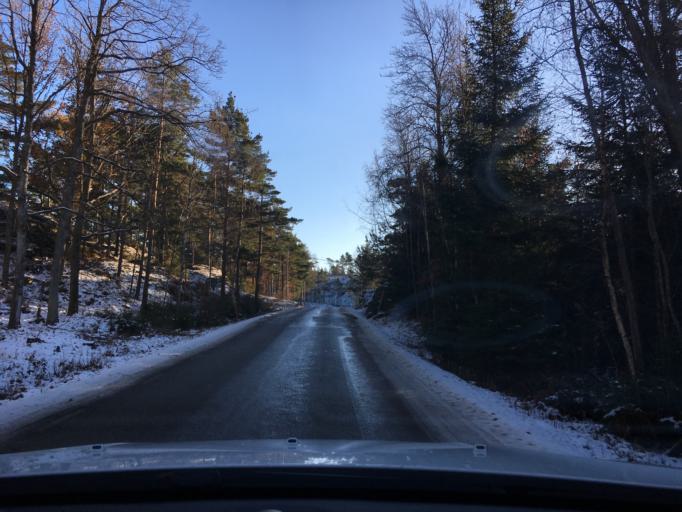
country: SE
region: Vaestra Goetaland
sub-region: Tjorns Kommun
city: Myggenas
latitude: 58.0961
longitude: 11.7164
